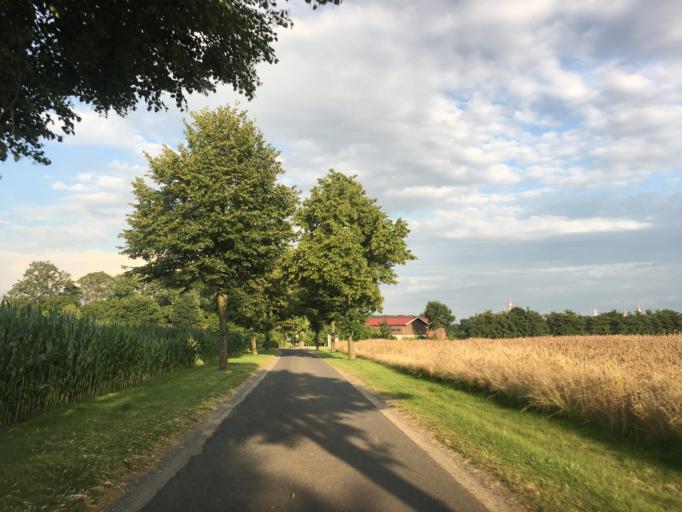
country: DE
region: North Rhine-Westphalia
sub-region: Regierungsbezirk Munster
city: Muenster
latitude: 51.9759
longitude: 7.5403
